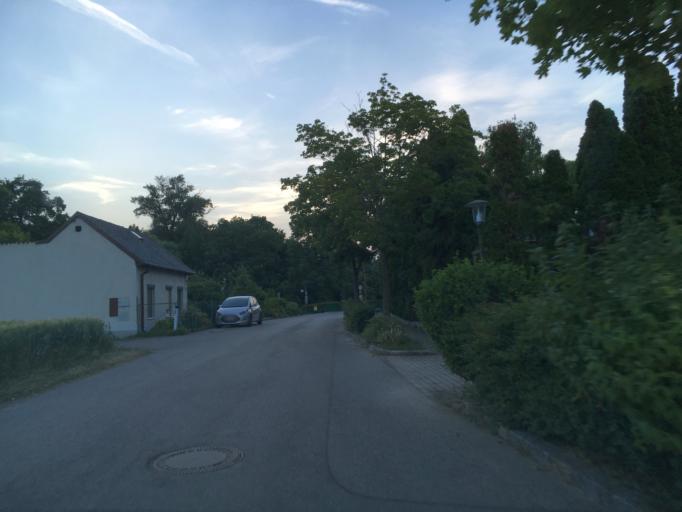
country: AT
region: Lower Austria
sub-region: Politischer Bezirk Baden
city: Teesdorf
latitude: 47.9489
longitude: 16.2760
